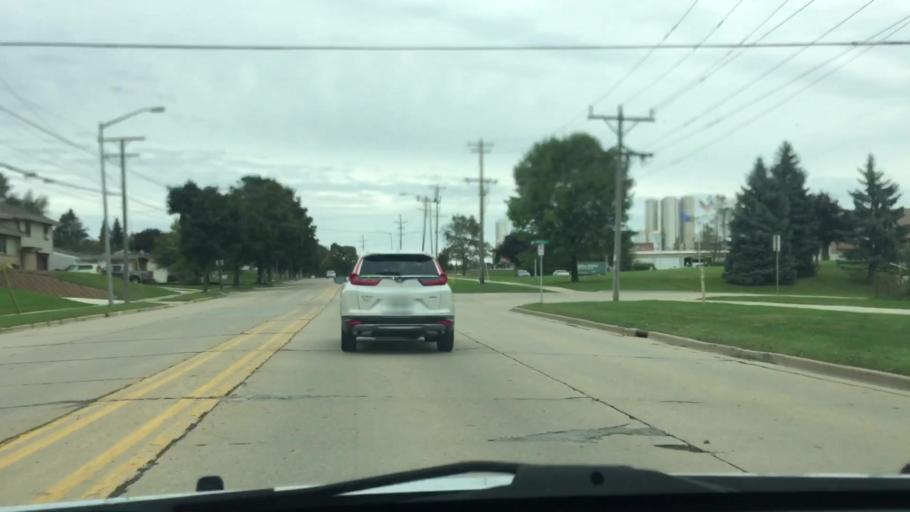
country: US
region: Wisconsin
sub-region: Waukesha County
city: Waukesha
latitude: 43.0284
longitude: -88.2428
